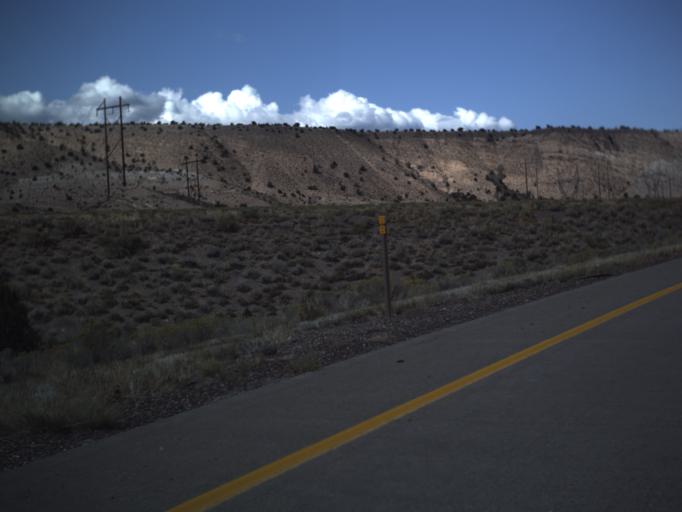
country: US
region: Utah
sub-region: Sevier County
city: Monroe
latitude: 38.5986
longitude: -112.2537
